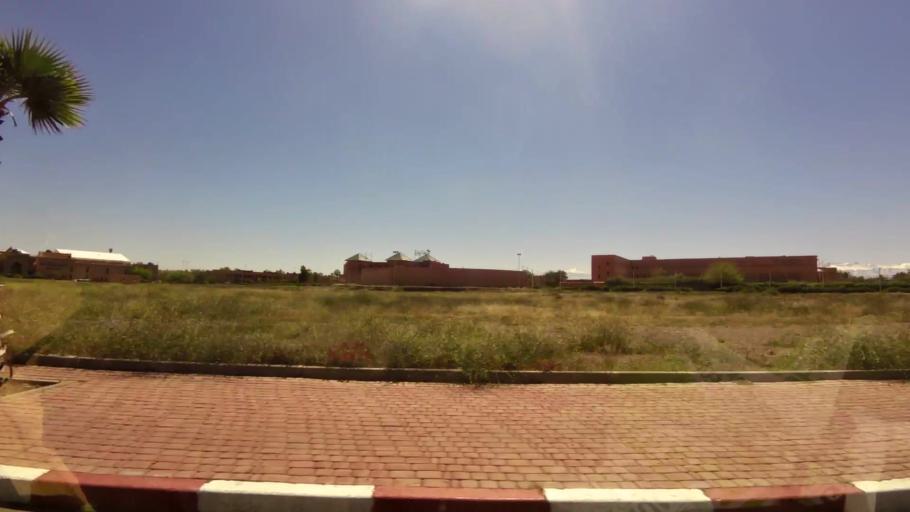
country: MA
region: Marrakech-Tensift-Al Haouz
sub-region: Marrakech
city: Marrakesh
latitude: 31.5956
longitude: -7.9925
